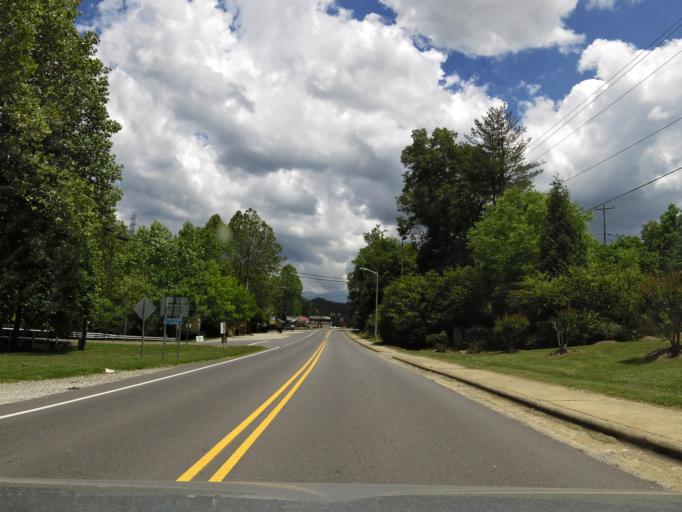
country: US
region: North Carolina
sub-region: Graham County
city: Robbinsville
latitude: 35.3289
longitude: -83.8101
